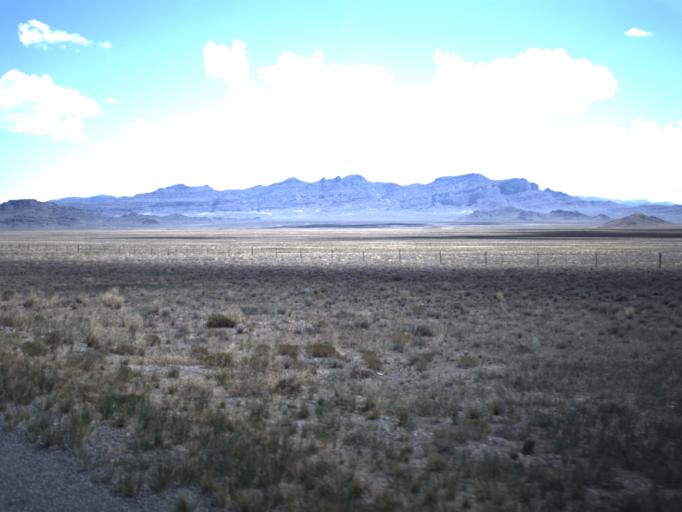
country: US
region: Utah
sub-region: Beaver County
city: Milford
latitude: 39.0474
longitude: -113.7928
